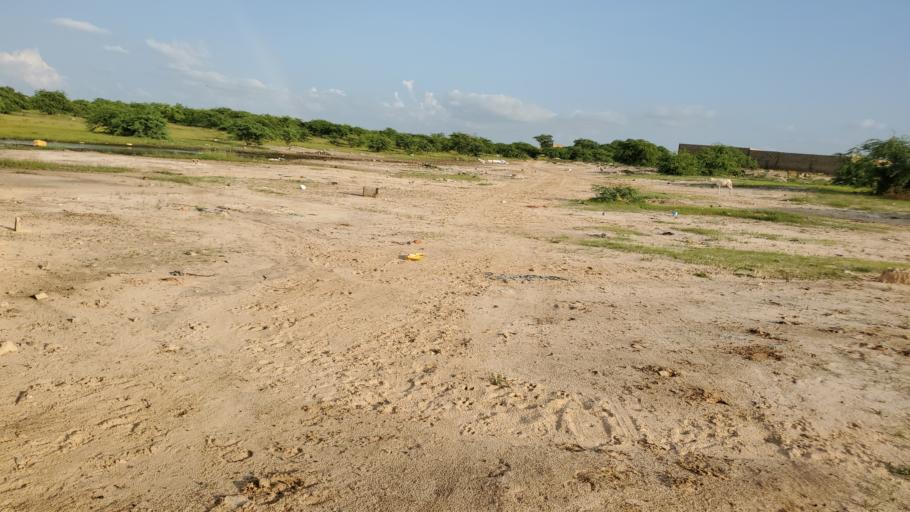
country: SN
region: Saint-Louis
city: Saint-Louis
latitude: 16.0514
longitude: -16.4207
